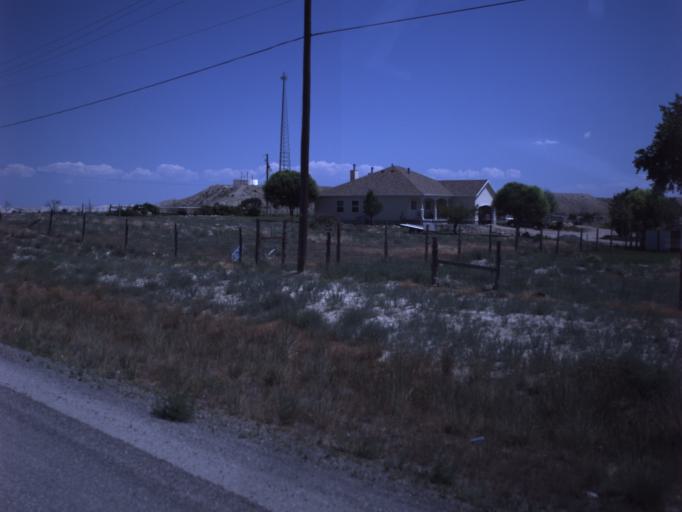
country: US
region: Utah
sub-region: Emery County
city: Ferron
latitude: 39.1010
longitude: -111.1312
